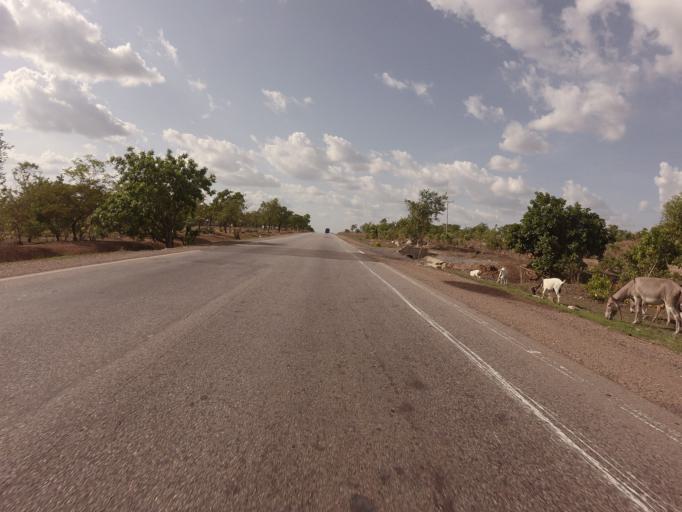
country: GH
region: Upper East
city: Bolgatanga
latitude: 10.5689
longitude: -0.8333
